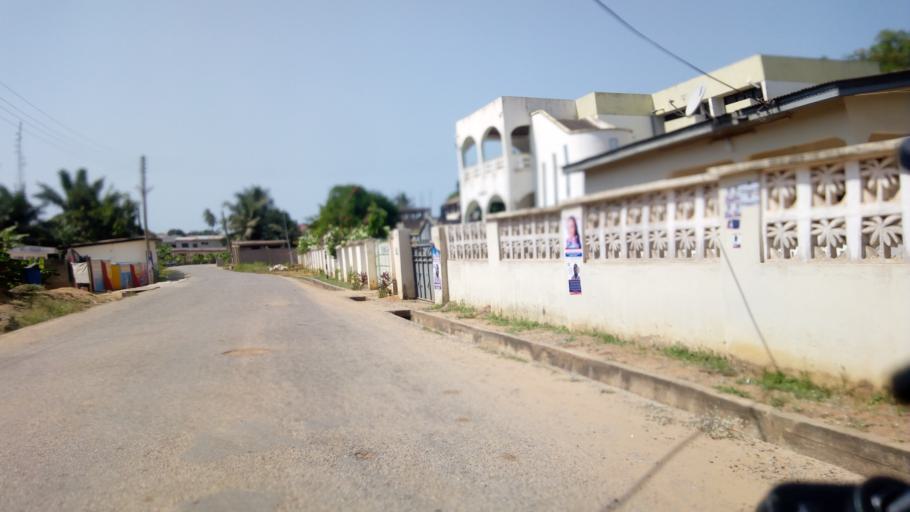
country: GH
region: Central
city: Cape Coast
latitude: 5.1100
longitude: -1.2713
